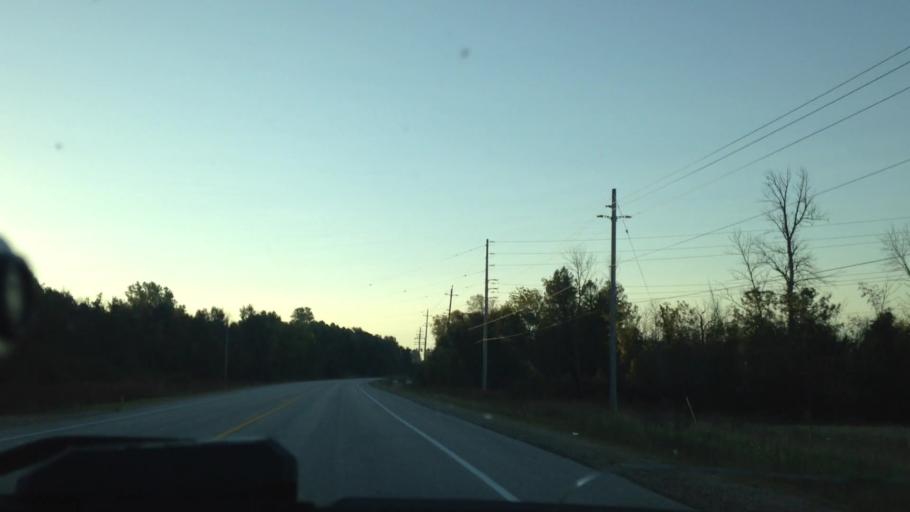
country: US
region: Wisconsin
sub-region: Washington County
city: Newburg
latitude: 43.4257
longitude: -88.0350
